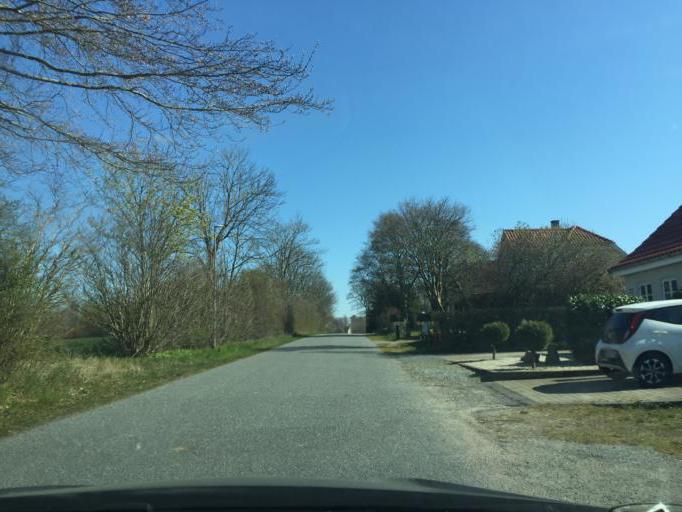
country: DK
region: South Denmark
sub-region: Faaborg-Midtfyn Kommune
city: Ringe
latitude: 55.2473
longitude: 10.4975
